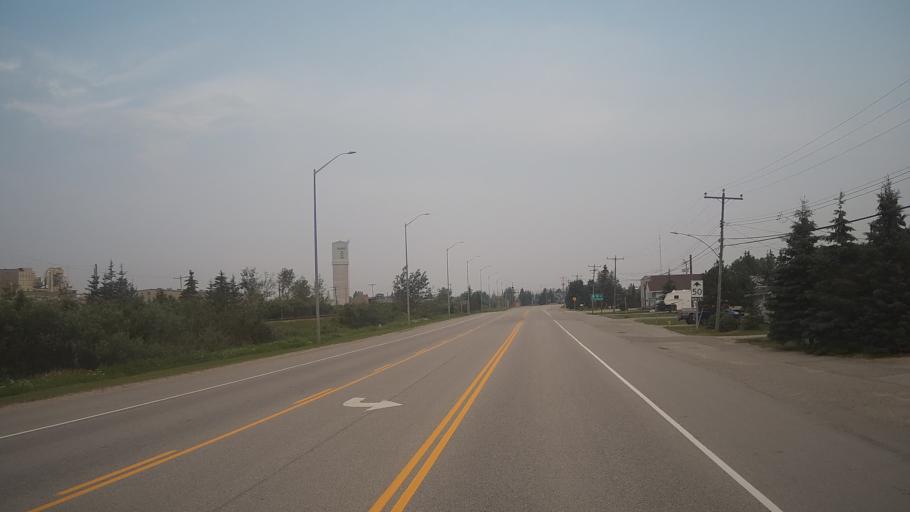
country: CA
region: Ontario
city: Hearst
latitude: 49.6873
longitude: -83.6435
